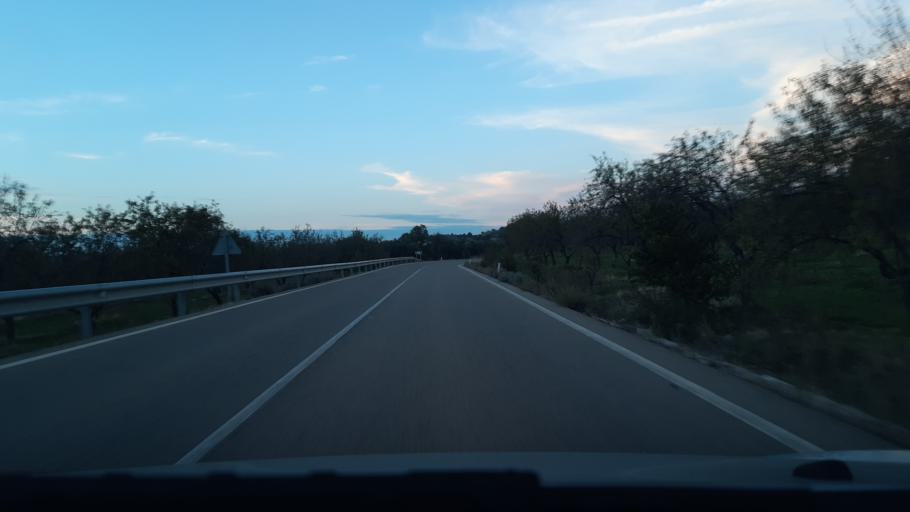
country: ES
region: Aragon
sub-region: Provincia de Teruel
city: Valderrobres
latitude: 40.8482
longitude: 0.1732
